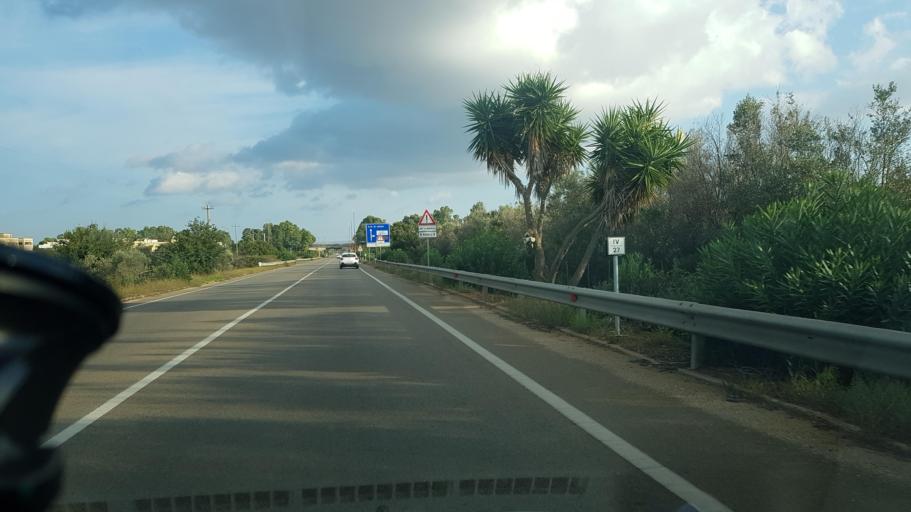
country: IT
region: Apulia
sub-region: Provincia di Lecce
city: Presicce
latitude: 39.8981
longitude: 18.2528
